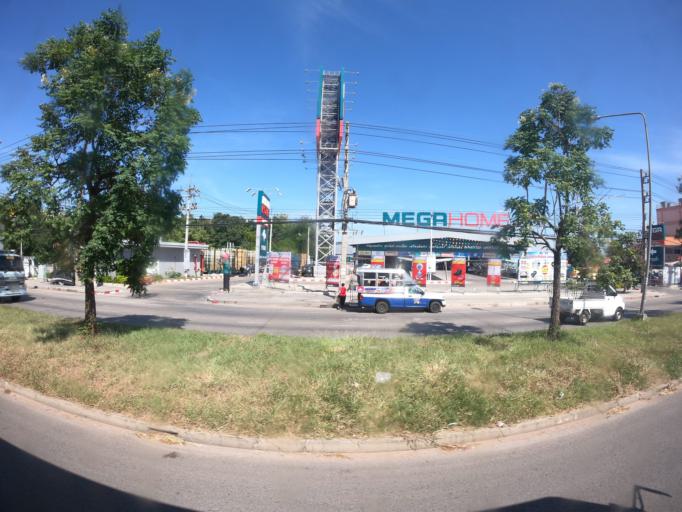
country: TH
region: Nakhon Ratchasima
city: Nakhon Ratchasima
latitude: 14.9963
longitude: 102.1072
